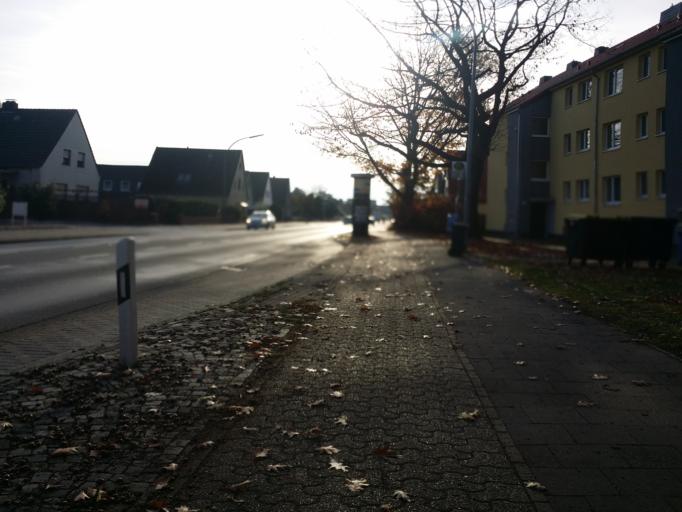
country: DE
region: Lower Saxony
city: Delmenhorst
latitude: 53.0341
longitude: 8.6505
